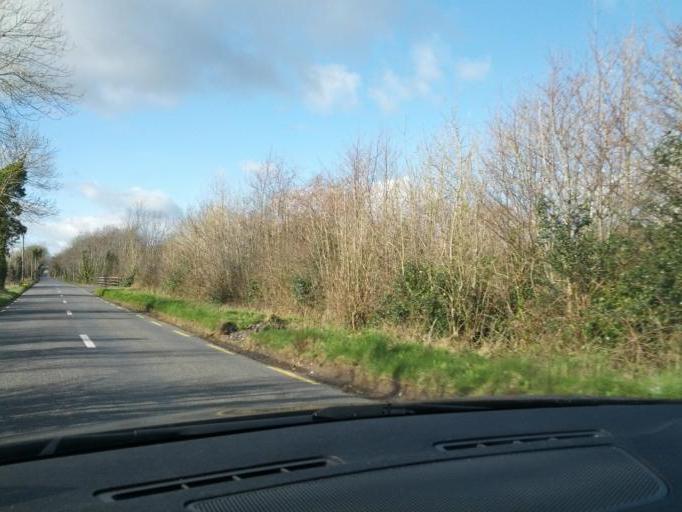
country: IE
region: Connaught
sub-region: County Galway
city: Athenry
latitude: 53.4958
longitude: -8.5681
